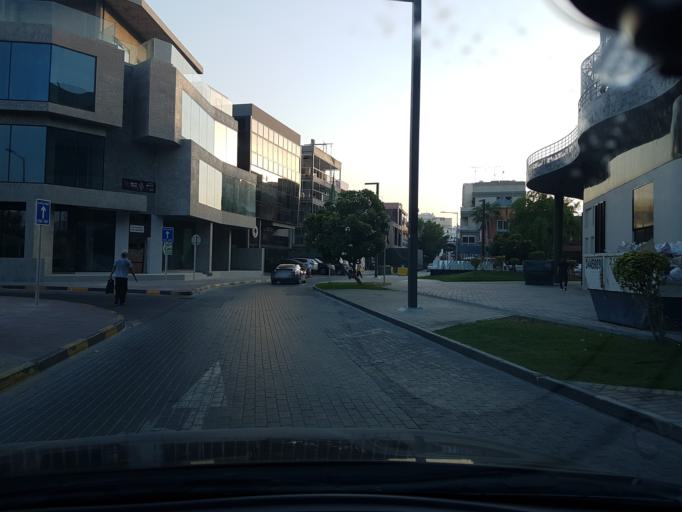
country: BH
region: Manama
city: Manama
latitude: 26.2143
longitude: 50.5938
